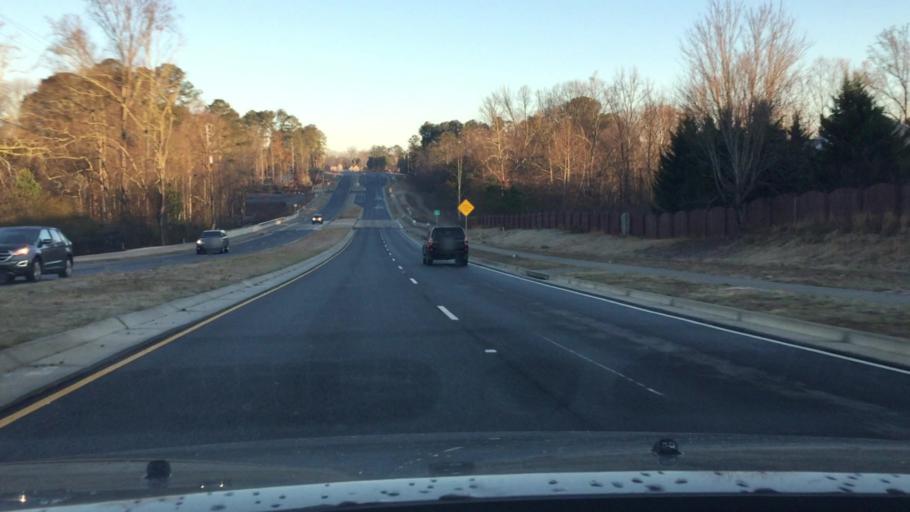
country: US
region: Georgia
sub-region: Forsyth County
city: Cumming
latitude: 34.1785
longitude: -84.1929
